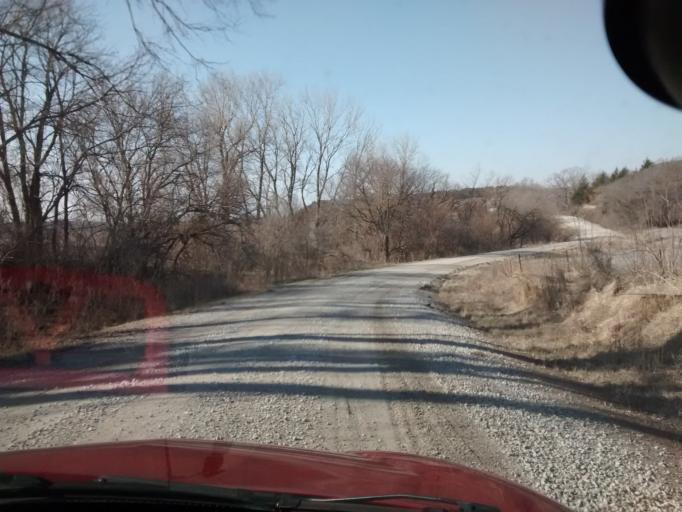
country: US
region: Iowa
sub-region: Pottawattamie County
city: Carter Lake
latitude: 41.4095
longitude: -95.8441
